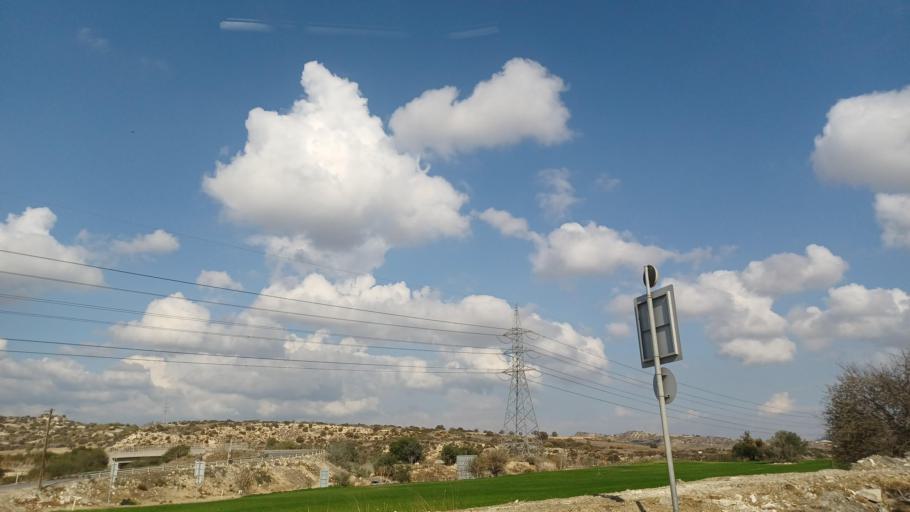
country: CY
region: Limassol
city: Pyrgos
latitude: 34.7448
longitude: 33.2935
